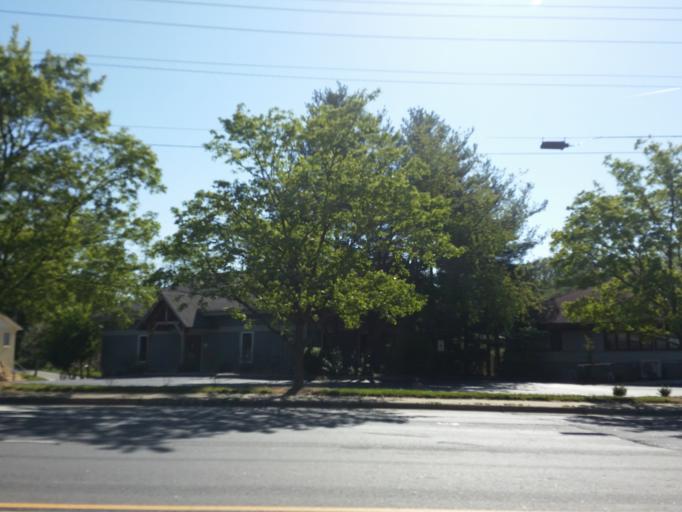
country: US
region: North Carolina
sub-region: Buncombe County
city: Asheville
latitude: 35.5821
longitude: -82.5544
